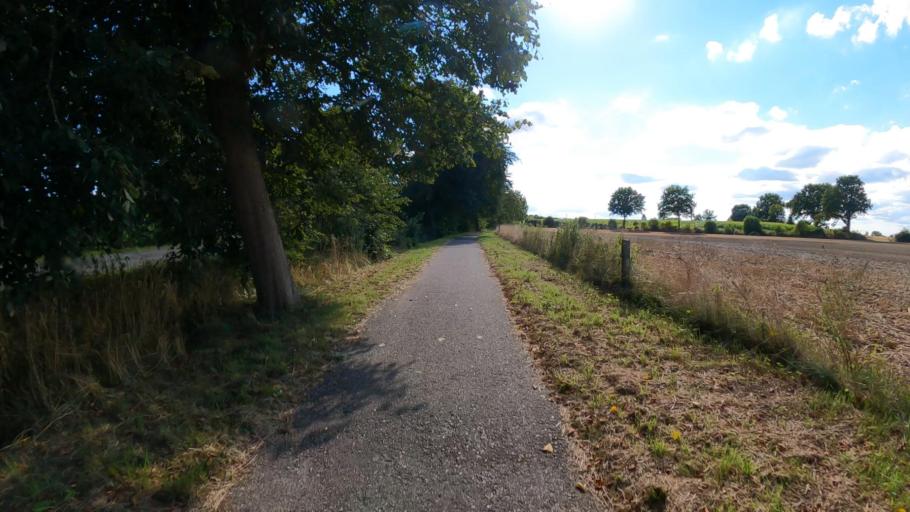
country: DE
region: Schleswig-Holstein
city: Lasbek
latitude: 53.7105
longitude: 10.3954
